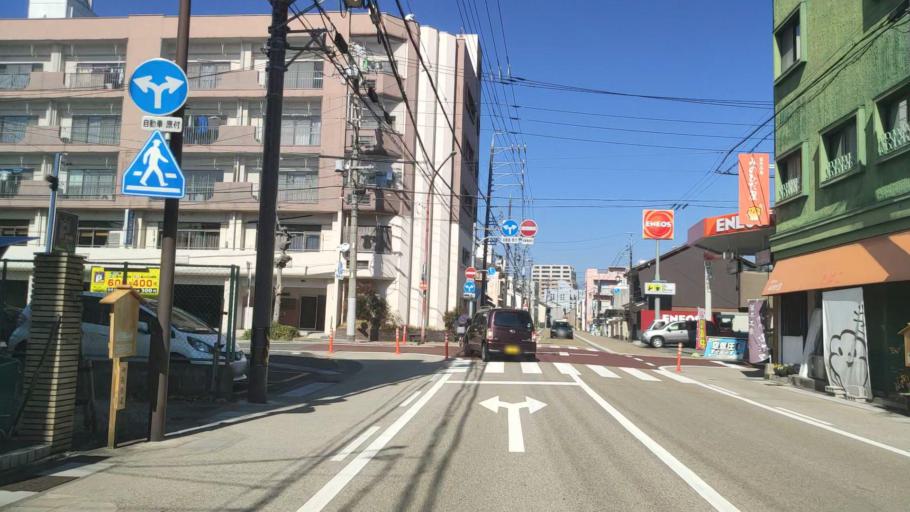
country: JP
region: Gifu
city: Gifu-shi
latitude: 35.4260
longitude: 136.7644
